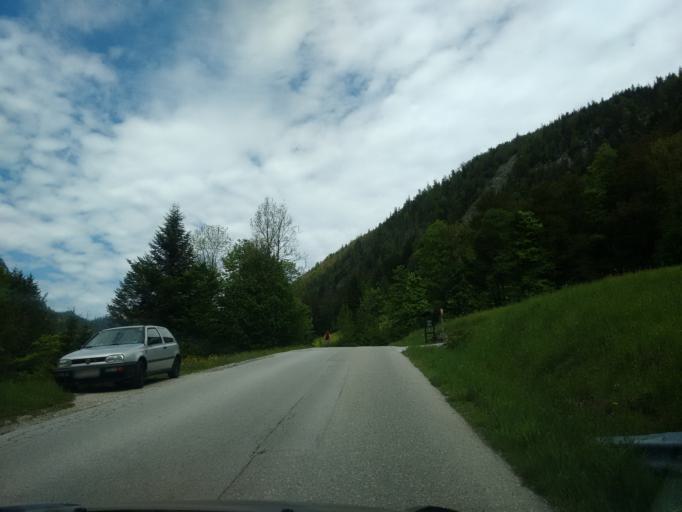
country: AT
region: Styria
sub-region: Politischer Bezirk Liezen
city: Altaussee
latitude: 47.6467
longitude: 13.7596
